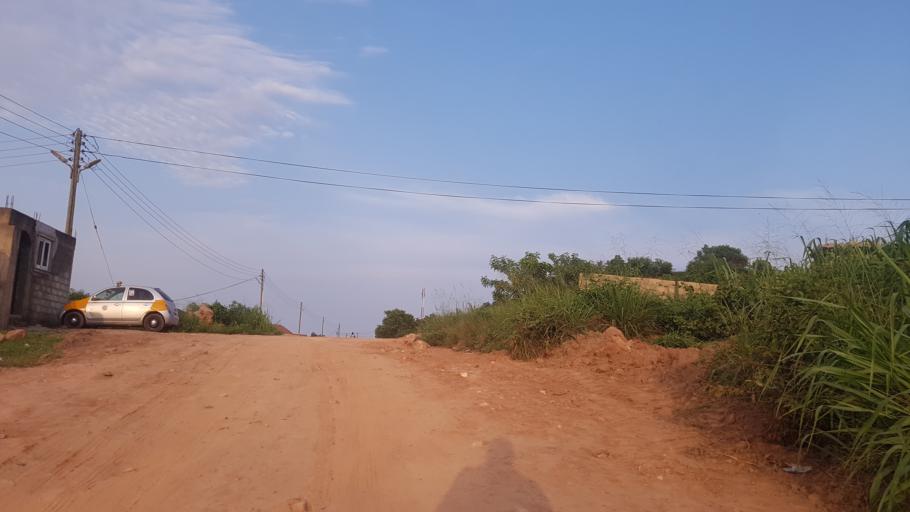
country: GH
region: Greater Accra
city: Gbawe
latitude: 5.5220
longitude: -0.3391
